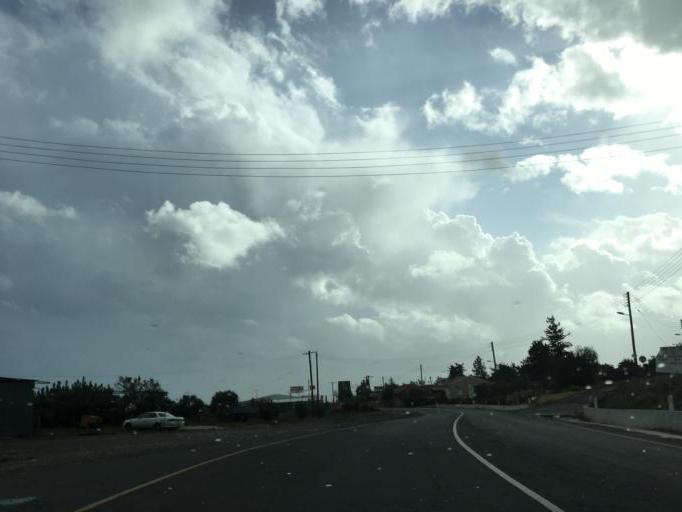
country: CY
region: Limassol
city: Erimi
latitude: 34.6710
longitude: 32.9122
